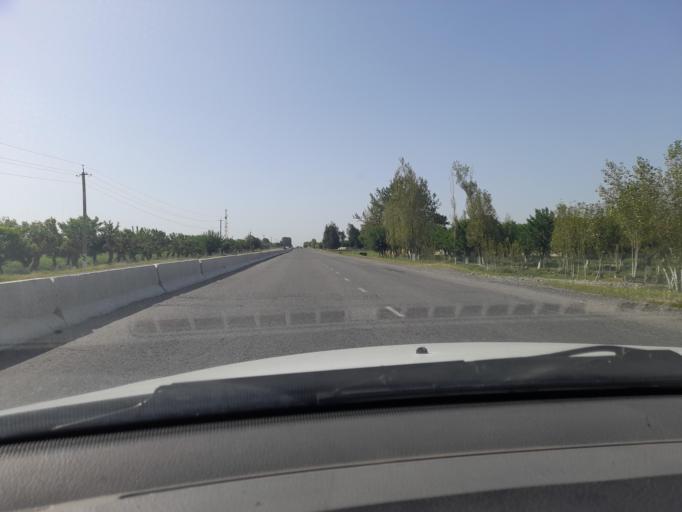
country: UZ
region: Samarqand
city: Daxbet
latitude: 39.8090
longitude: 66.8573
